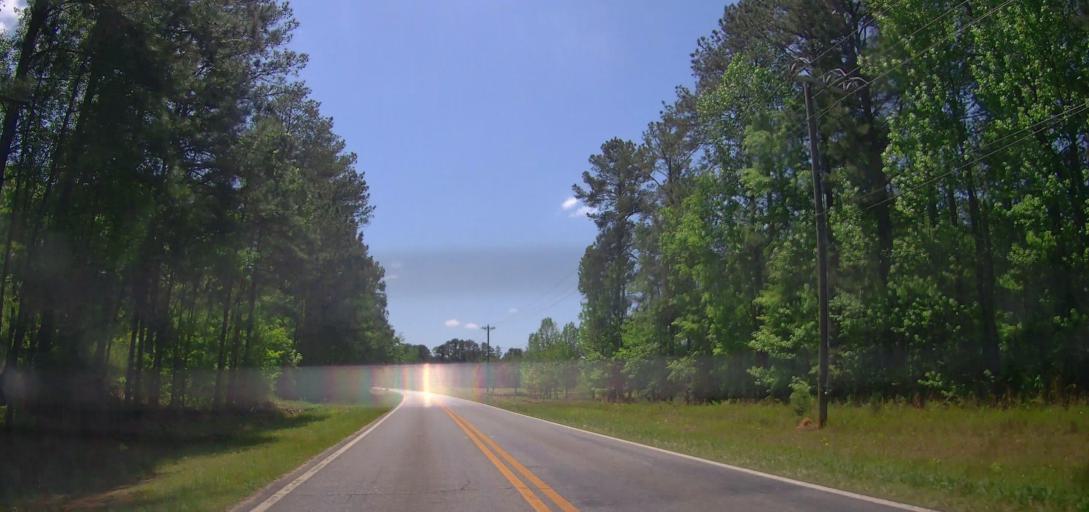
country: US
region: Georgia
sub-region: Jones County
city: Gray
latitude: 32.9712
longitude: -83.5480
